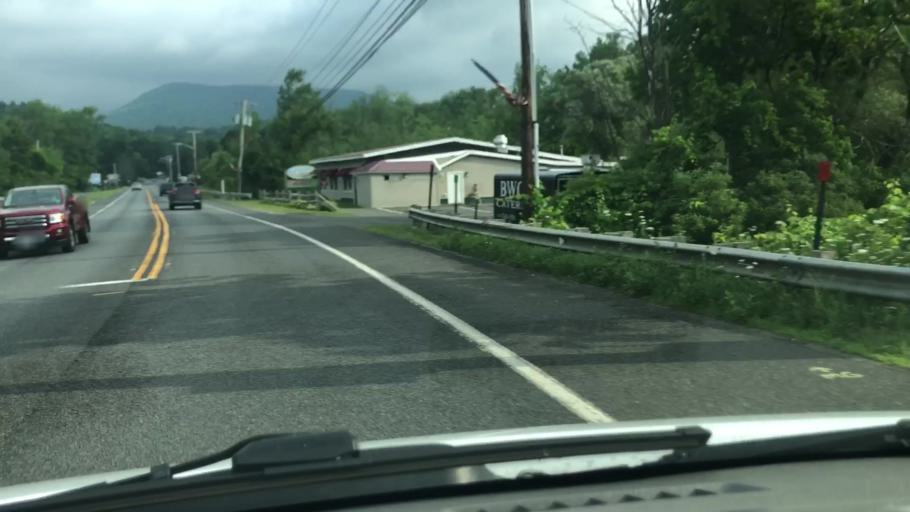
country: US
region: Massachusetts
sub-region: Berkshire County
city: Lanesborough
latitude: 42.5542
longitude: -73.1652
